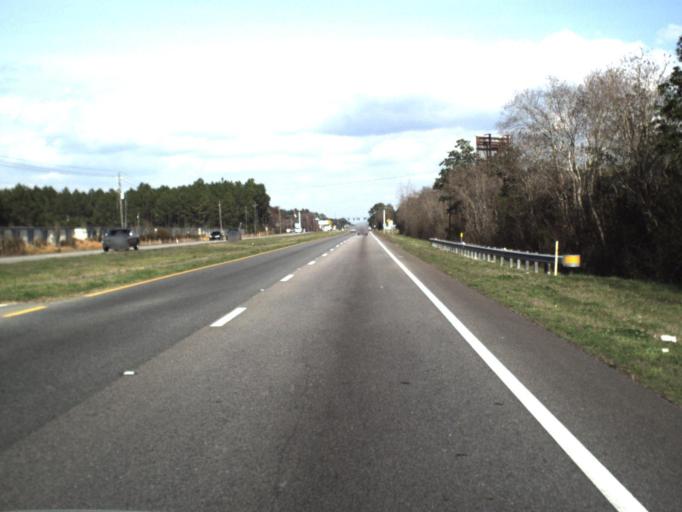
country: US
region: Florida
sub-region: Bay County
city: Hiland Park
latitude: 30.2382
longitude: -85.5719
